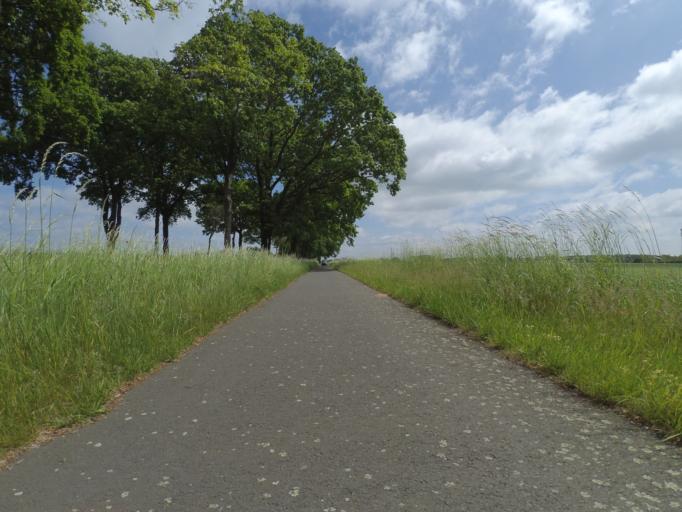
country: DE
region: Lower Saxony
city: Edemissen
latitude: 52.3980
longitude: 10.3114
